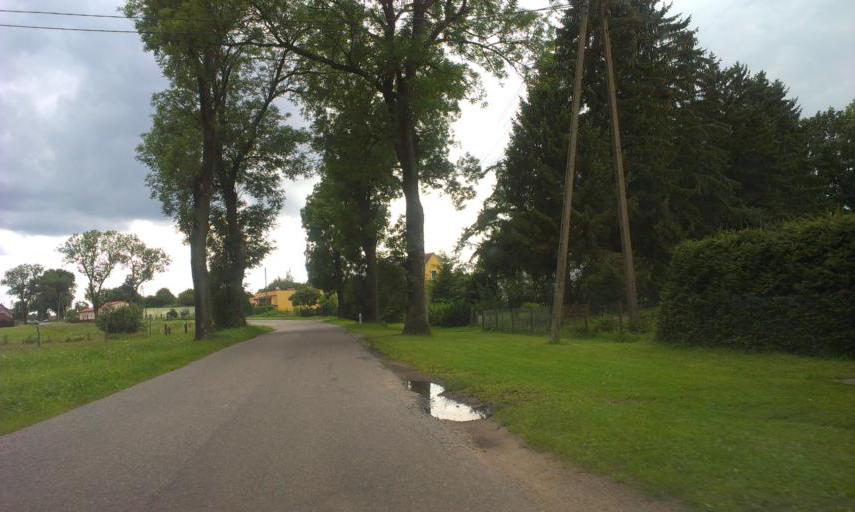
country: PL
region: West Pomeranian Voivodeship
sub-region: Powiat bialogardzki
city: Tychowo
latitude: 53.8976
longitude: 16.2082
